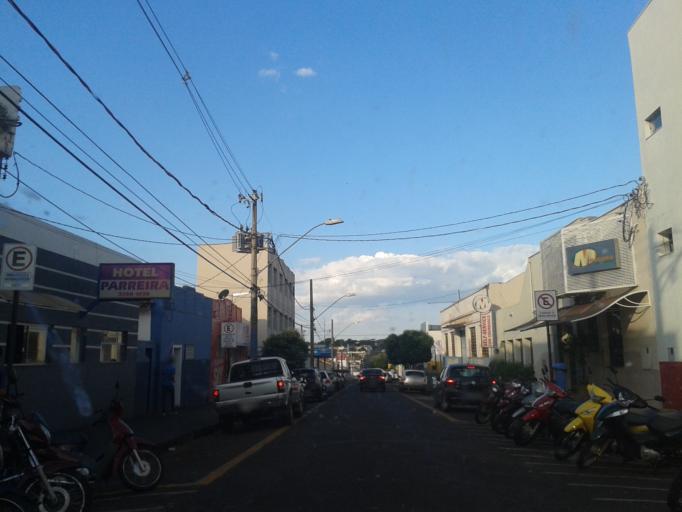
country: BR
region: Minas Gerais
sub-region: Ituiutaba
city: Ituiutaba
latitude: -18.9715
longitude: -49.4630
